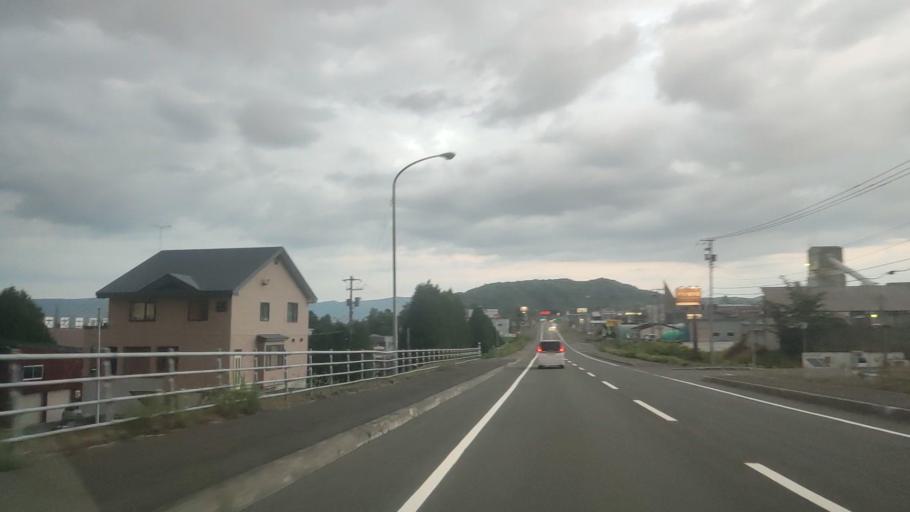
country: JP
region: Hokkaido
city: Shimo-furano
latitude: 43.3519
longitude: 142.3661
